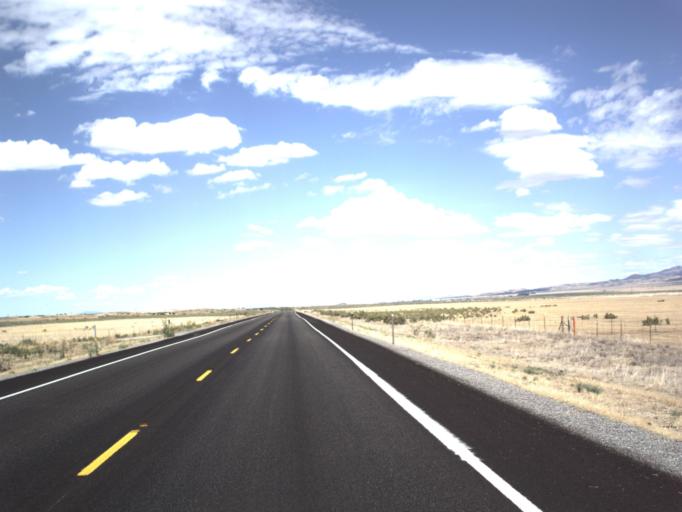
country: US
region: Utah
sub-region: Millard County
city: Fillmore
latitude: 39.1231
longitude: -112.3576
